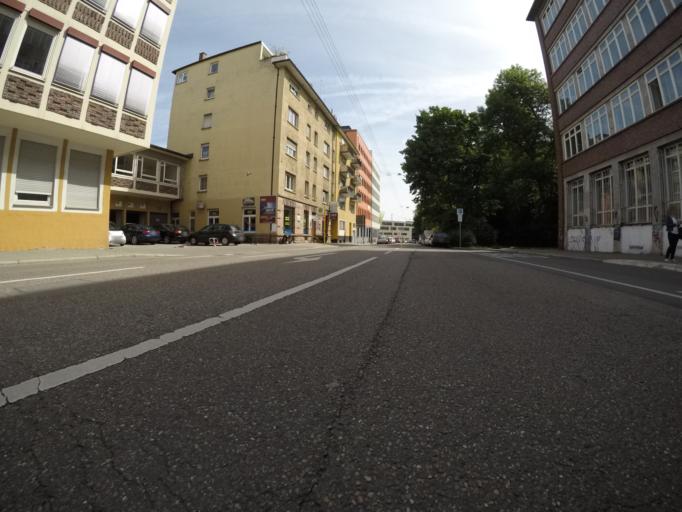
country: DE
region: Baden-Wuerttemberg
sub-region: Regierungsbezirk Stuttgart
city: Stuttgart
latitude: 48.7816
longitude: 9.1657
